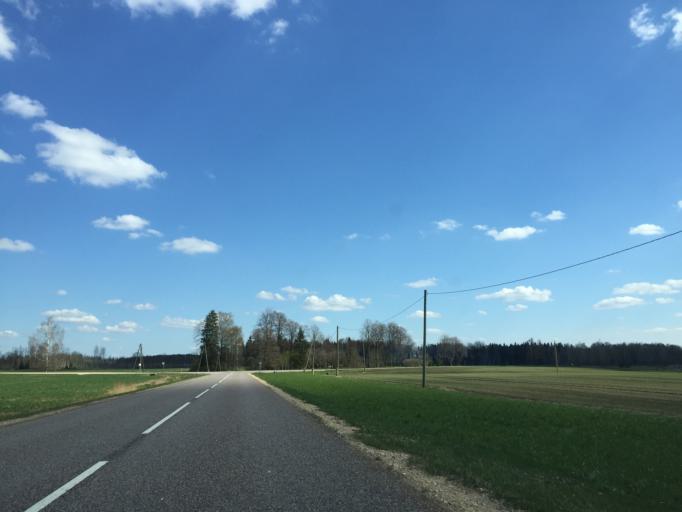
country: LV
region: Saulkrastu
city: Saulkrasti
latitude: 57.2495
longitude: 24.5138
